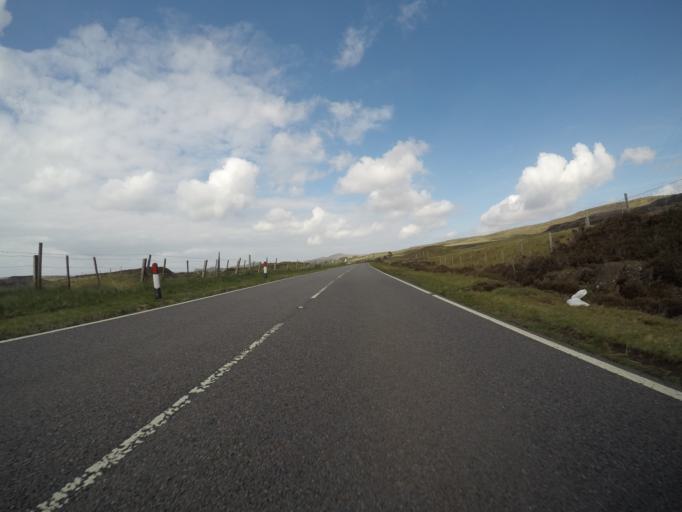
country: GB
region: Scotland
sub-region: Highland
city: Portree
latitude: 57.5533
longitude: -6.3658
